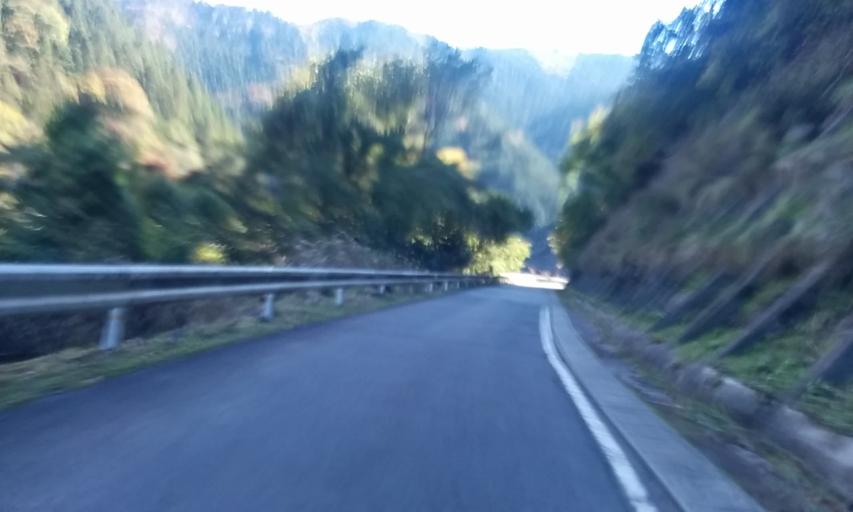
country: JP
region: Kyoto
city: Kameoka
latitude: 35.1301
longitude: 135.5643
